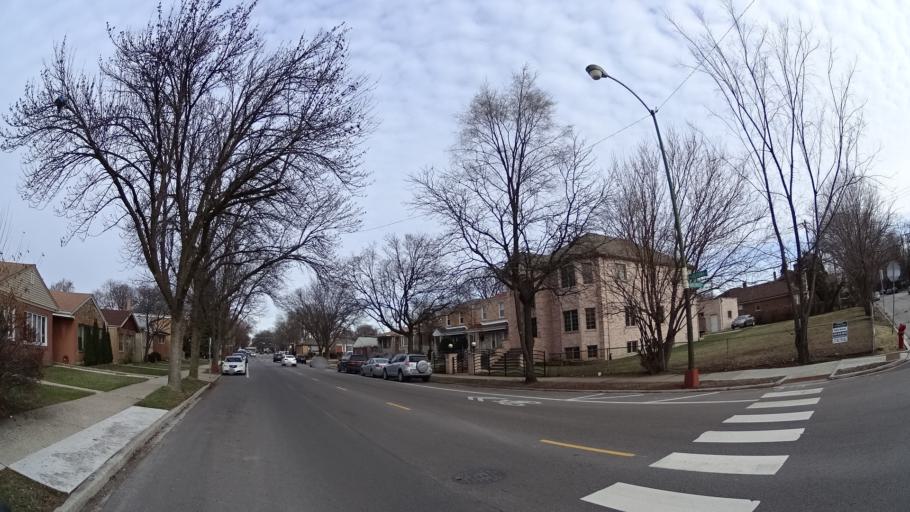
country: US
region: Illinois
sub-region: Cook County
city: Evanston
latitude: 42.0176
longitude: -87.6997
